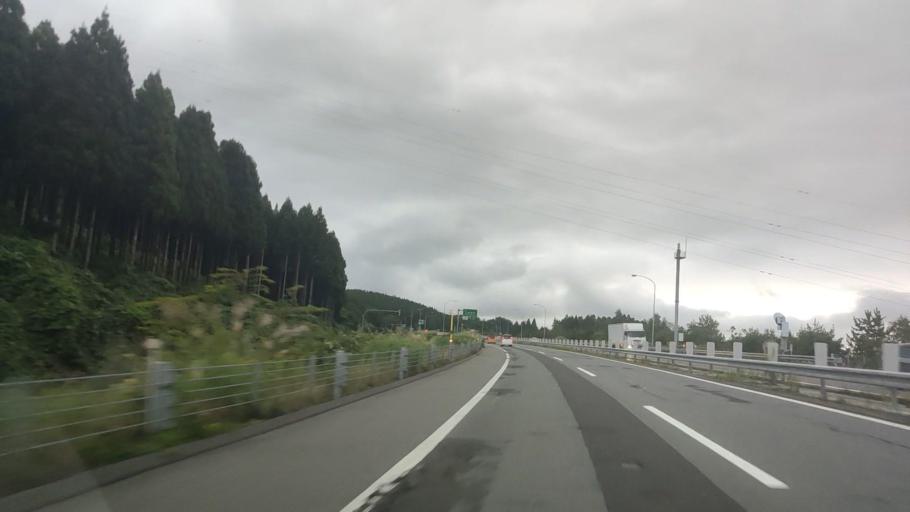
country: JP
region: Hokkaido
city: Nanae
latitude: 41.9022
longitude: 140.7001
